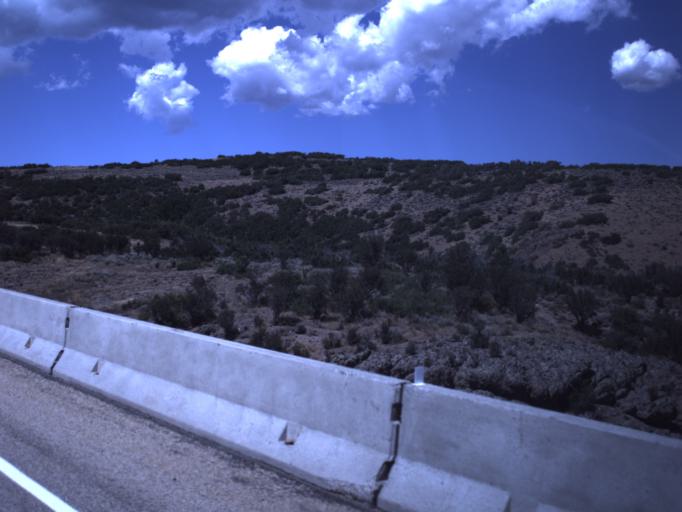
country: US
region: Utah
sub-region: Wasatch County
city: Heber
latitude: 40.5898
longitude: -111.3834
